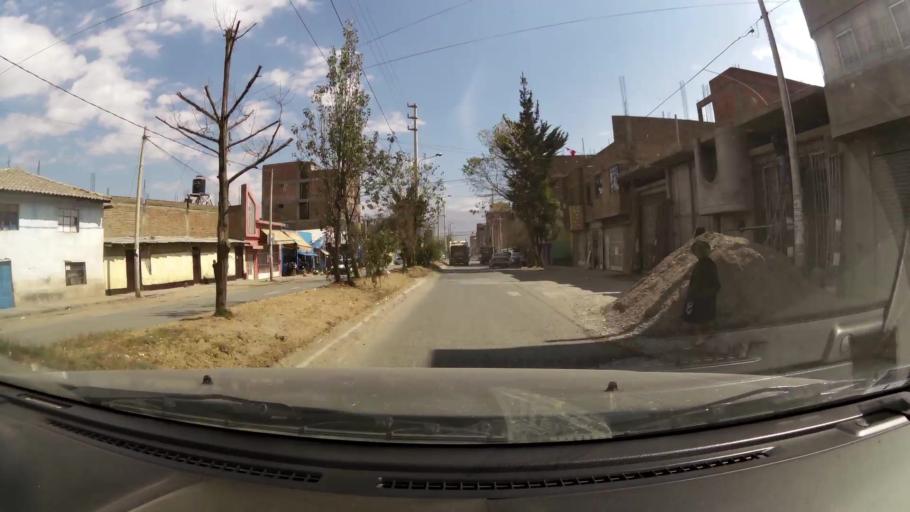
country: PE
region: Junin
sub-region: Provincia de Huancayo
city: Huancayo
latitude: -12.0872
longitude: -75.2015
